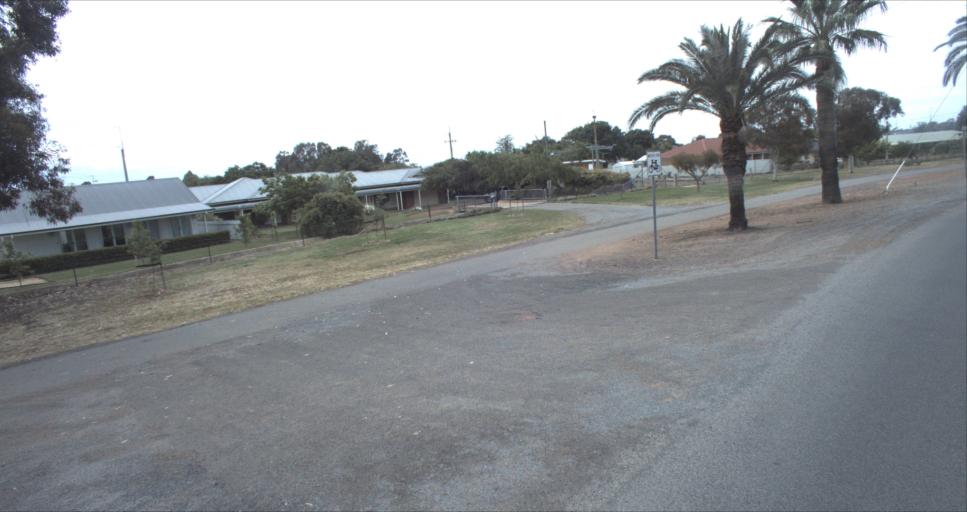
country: AU
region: New South Wales
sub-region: Leeton
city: Leeton
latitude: -34.5452
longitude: 146.4105
